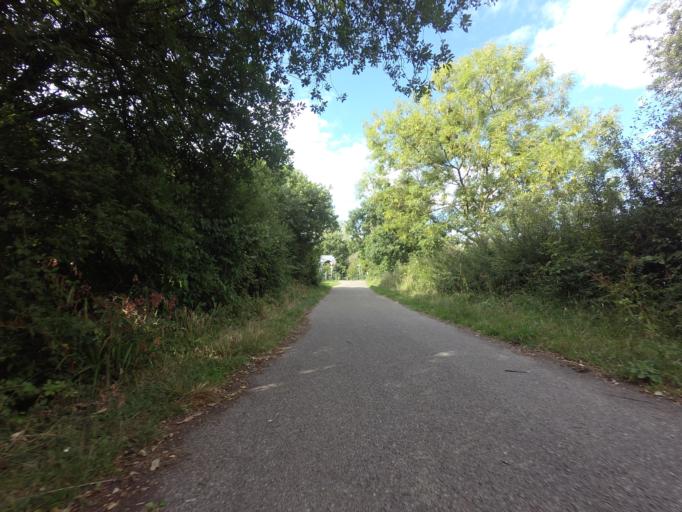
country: GB
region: England
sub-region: East Sussex
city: Hailsham
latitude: 50.8449
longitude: 0.2546
